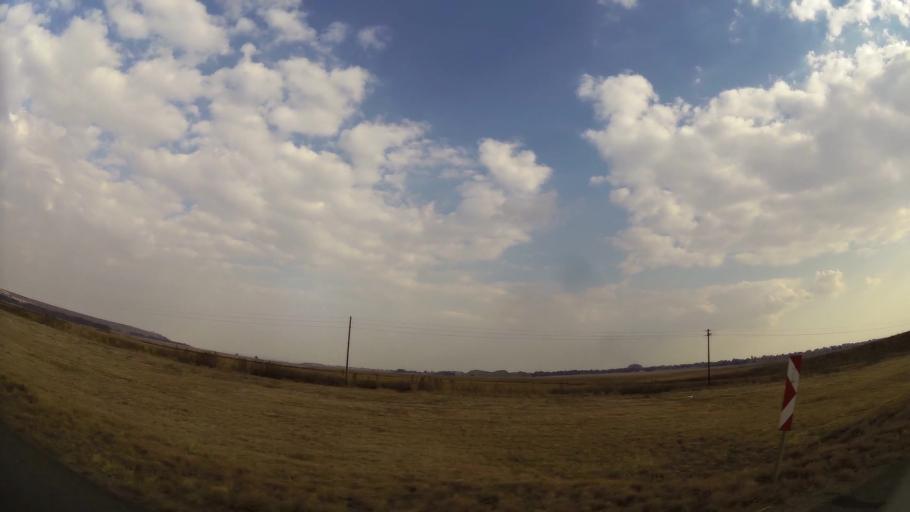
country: ZA
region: Gauteng
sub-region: Ekurhuleni Metropolitan Municipality
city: Springs
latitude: -26.2725
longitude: 28.5079
